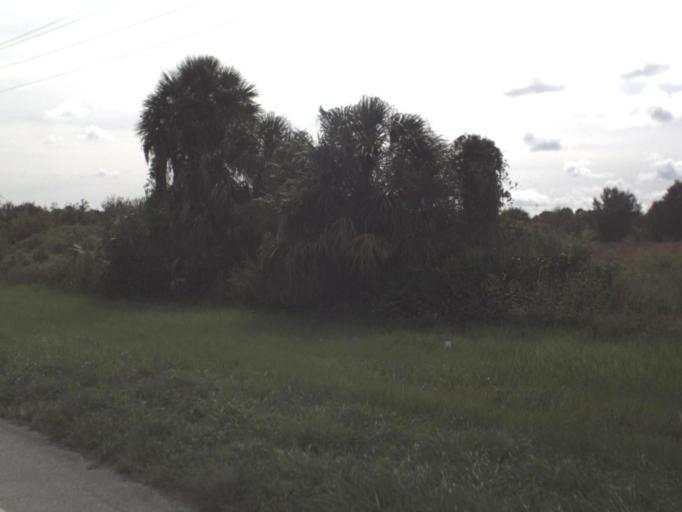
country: US
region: Florida
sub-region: Highlands County
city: Placid Lakes
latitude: 27.2091
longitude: -81.4529
